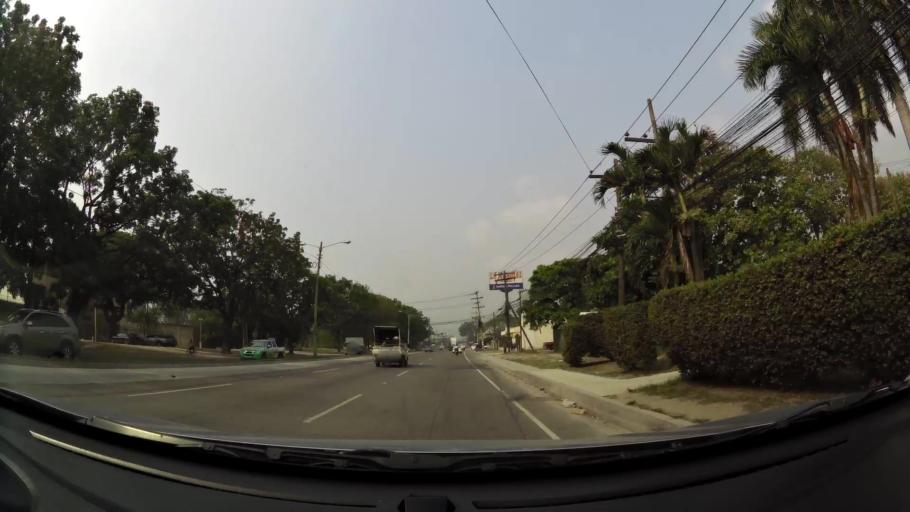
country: HN
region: Cortes
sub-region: San Pedro Sula
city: Pena Blanca
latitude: 15.5370
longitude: -88.0173
